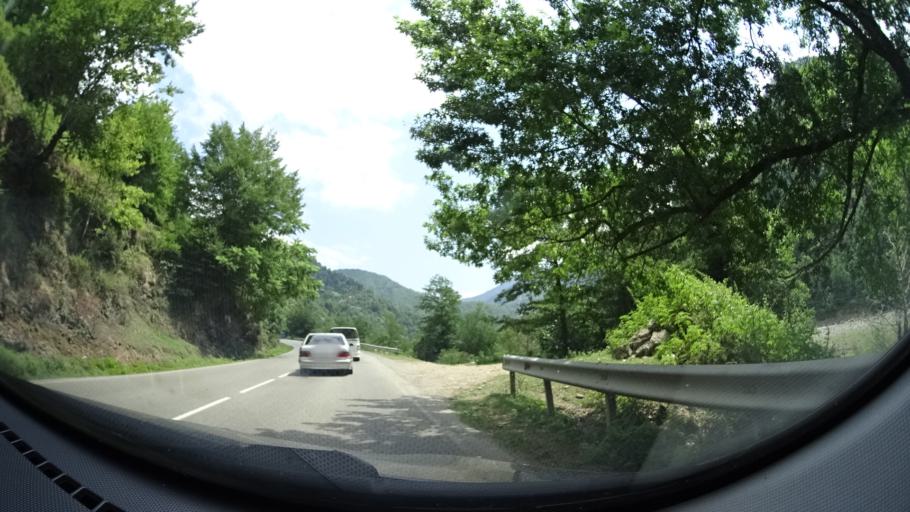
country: GE
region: Ajaria
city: Keda
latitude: 41.5678
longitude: 41.8430
